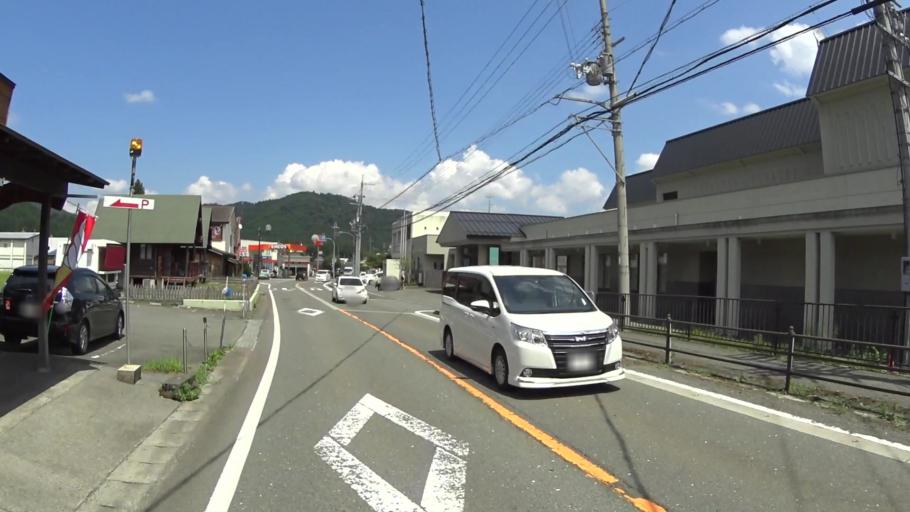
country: JP
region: Shiga Prefecture
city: Kitahama
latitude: 35.3514
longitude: 135.9152
